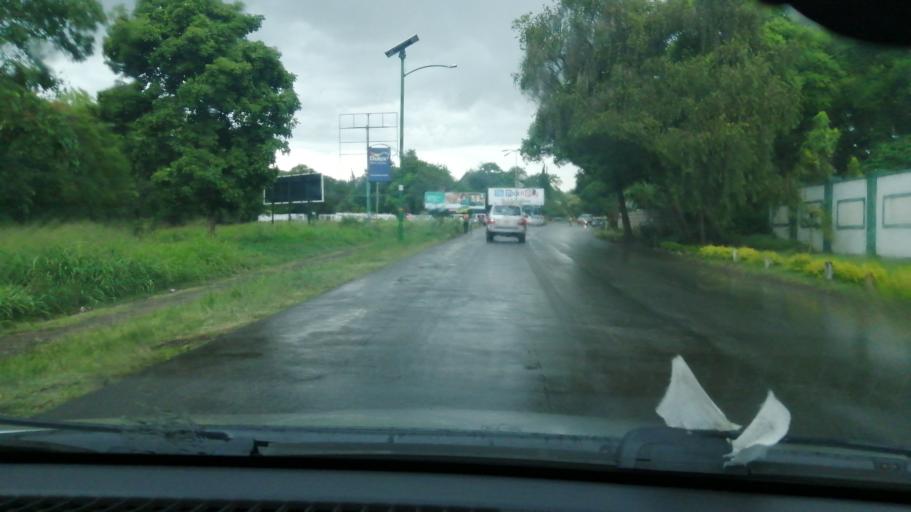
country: ZW
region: Harare
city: Harare
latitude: -17.7900
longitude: 31.0612
